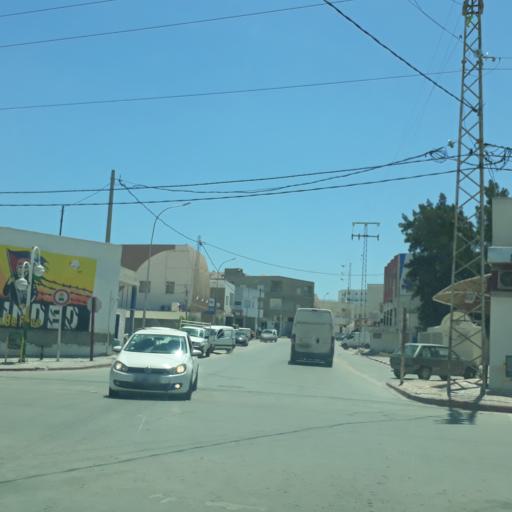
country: TN
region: Safaqis
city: Al Qarmadah
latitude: 34.8030
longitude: 10.7605
